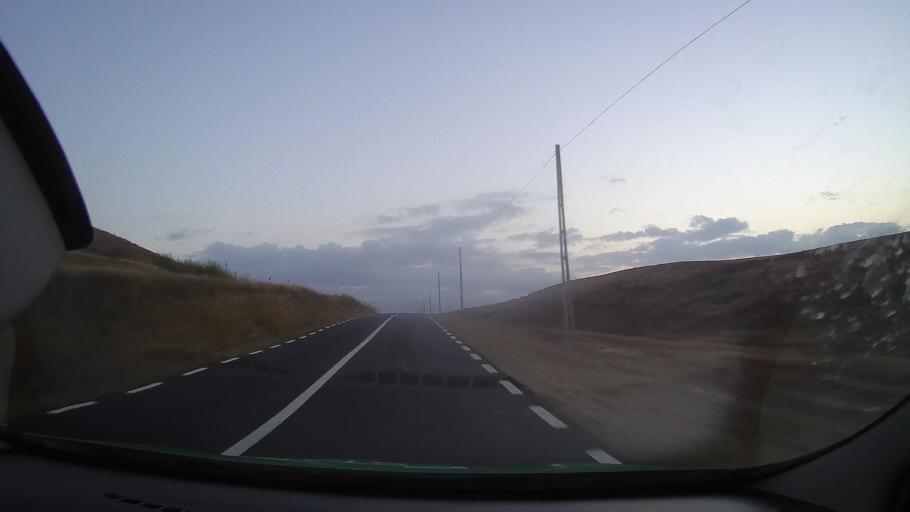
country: RO
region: Constanta
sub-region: Comuna Oltina
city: Oltina
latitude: 44.1460
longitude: 27.6666
